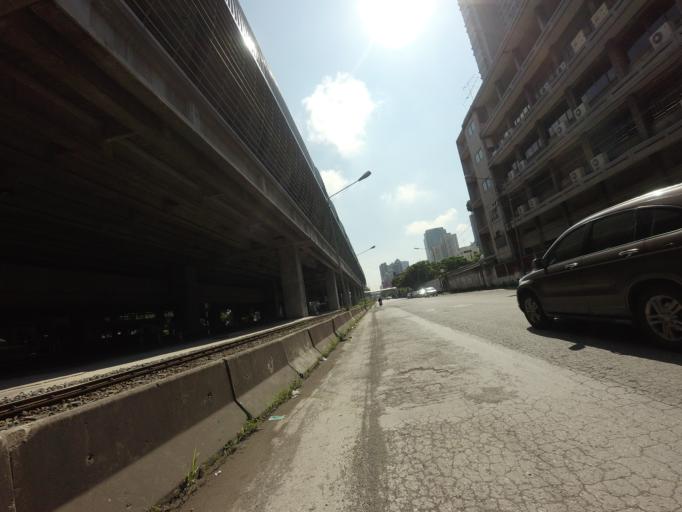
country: TH
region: Bangkok
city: Din Daeng
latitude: 13.7506
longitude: 100.5613
